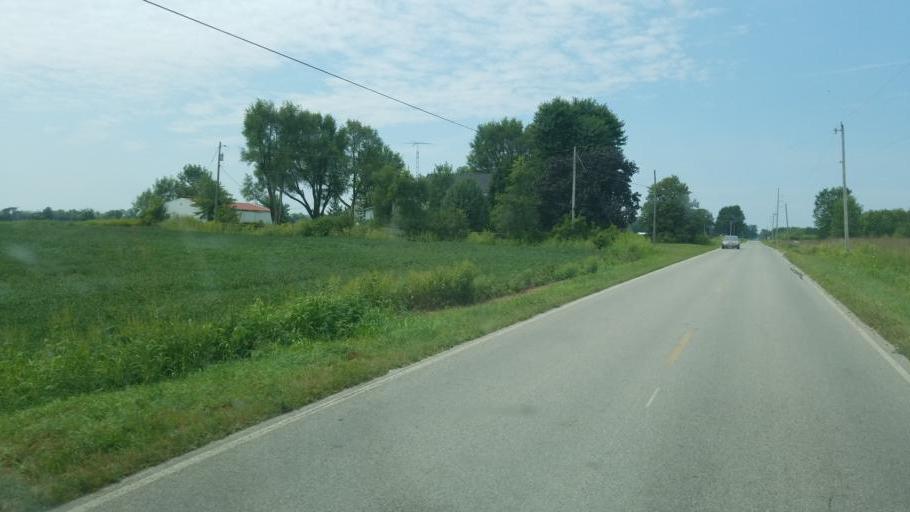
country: US
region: Ohio
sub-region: Marion County
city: Marion
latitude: 40.5714
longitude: -83.1854
